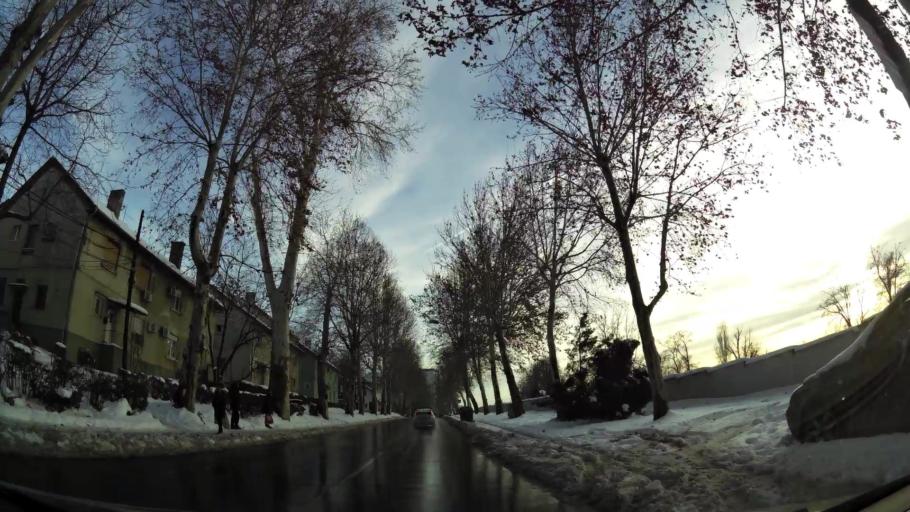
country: RS
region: Central Serbia
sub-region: Belgrade
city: Palilula
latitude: 44.8083
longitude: 20.4938
